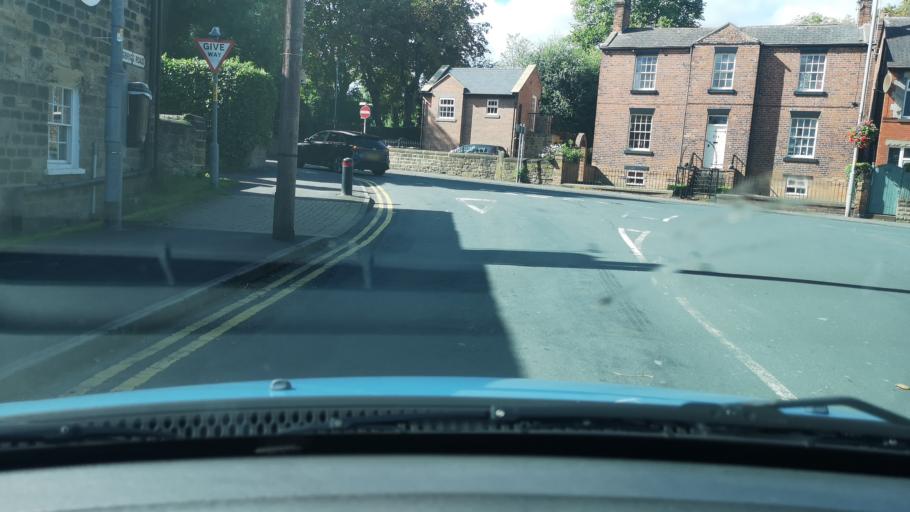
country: GB
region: England
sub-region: City and Borough of Wakefield
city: Walton
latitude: 53.6620
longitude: -1.4840
